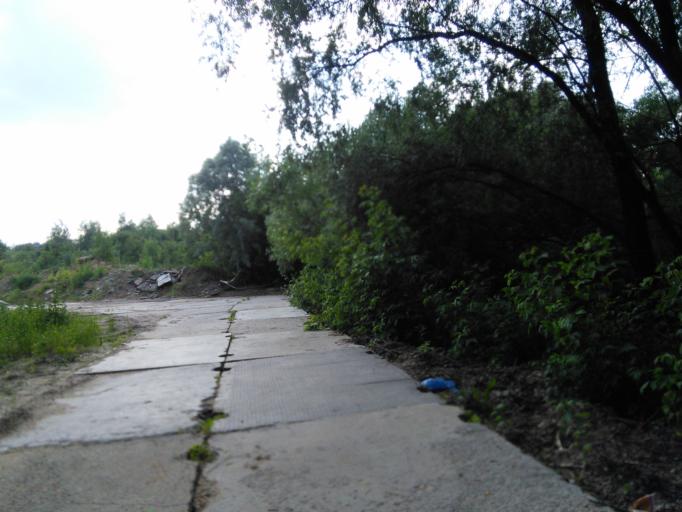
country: RU
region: Moskovskaya
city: Bogorodskoye
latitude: 55.8100
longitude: 37.6988
